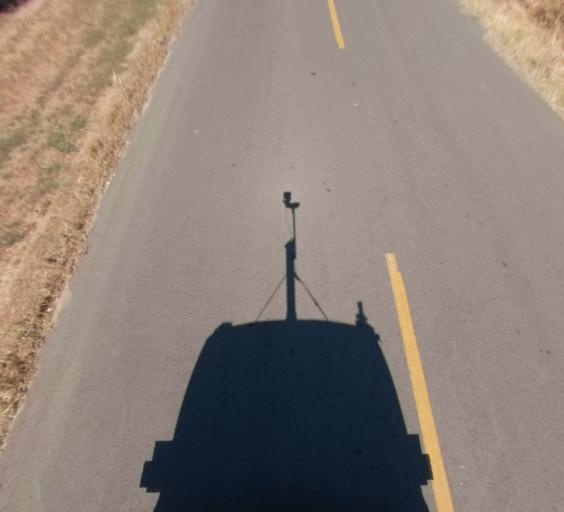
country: US
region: California
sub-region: Madera County
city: Parksdale
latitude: 36.9853
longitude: -120.0158
